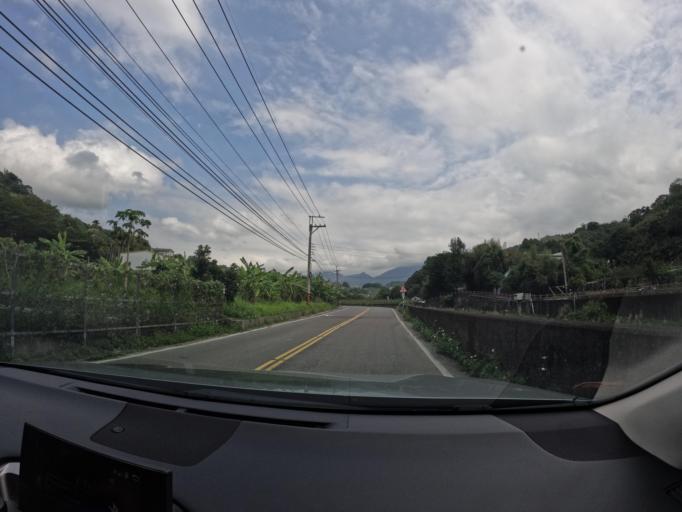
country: TW
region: Taiwan
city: Fengyuan
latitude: 24.3055
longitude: 120.8445
